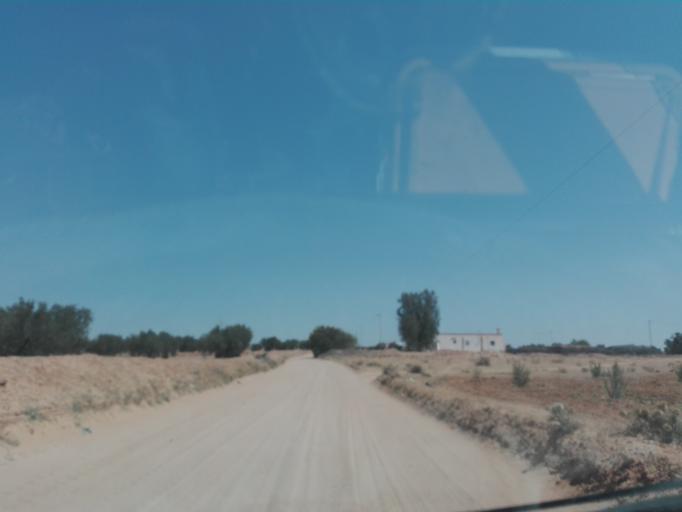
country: TN
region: Safaqis
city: Bi'r `Ali Bin Khalifah
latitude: 34.6604
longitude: 10.2410
